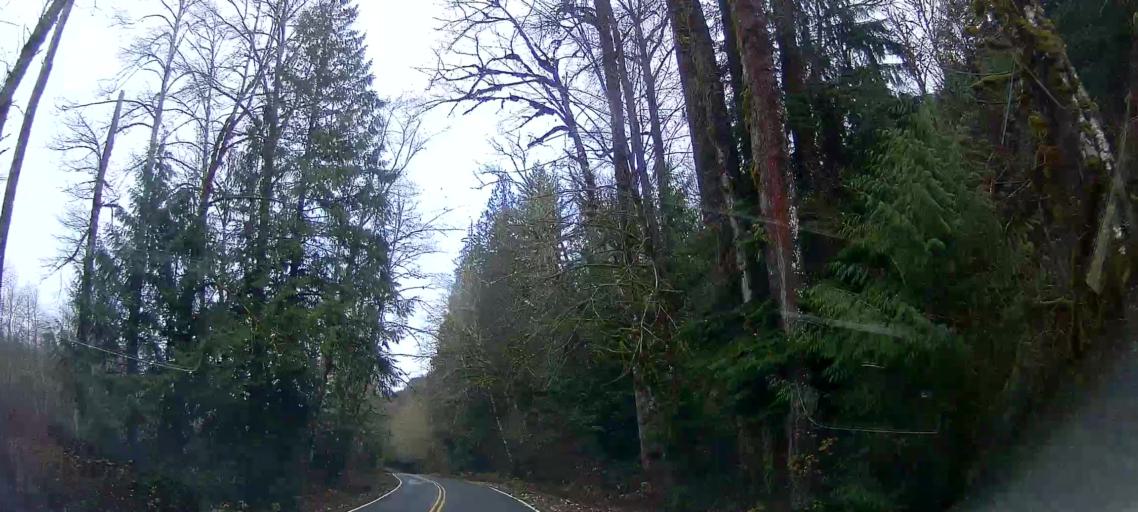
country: US
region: Washington
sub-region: Snohomish County
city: Darrington
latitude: 48.4976
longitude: -121.4647
